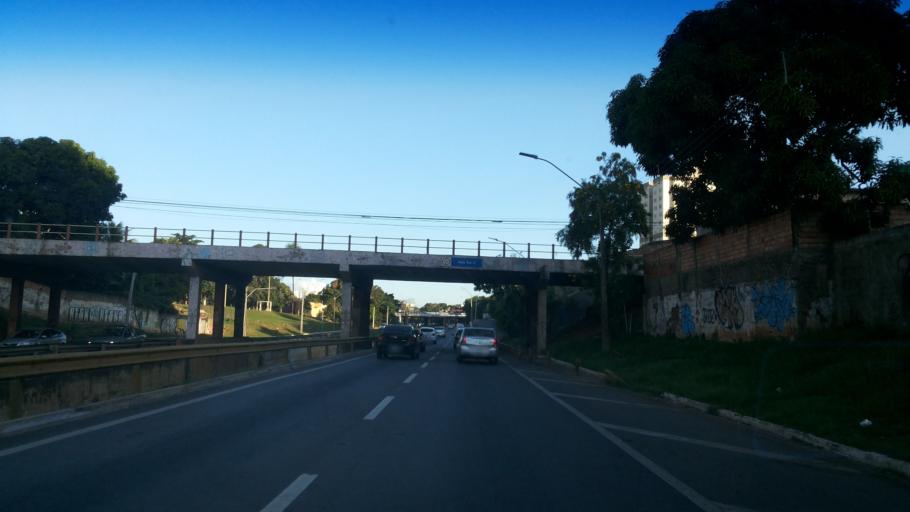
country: BR
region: Goias
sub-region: Goiania
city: Goiania
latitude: -16.6748
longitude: -49.2500
